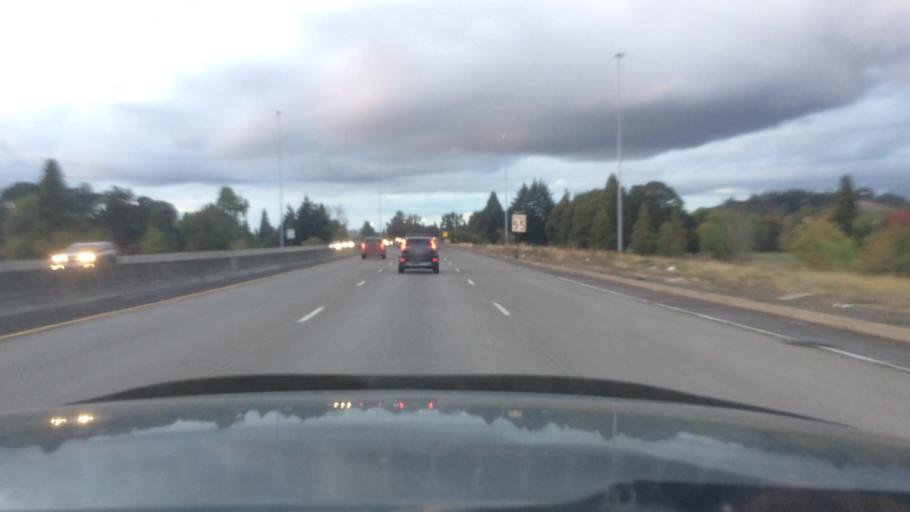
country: US
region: Oregon
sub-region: Lane County
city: Eugene
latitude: 44.0592
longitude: -123.1010
